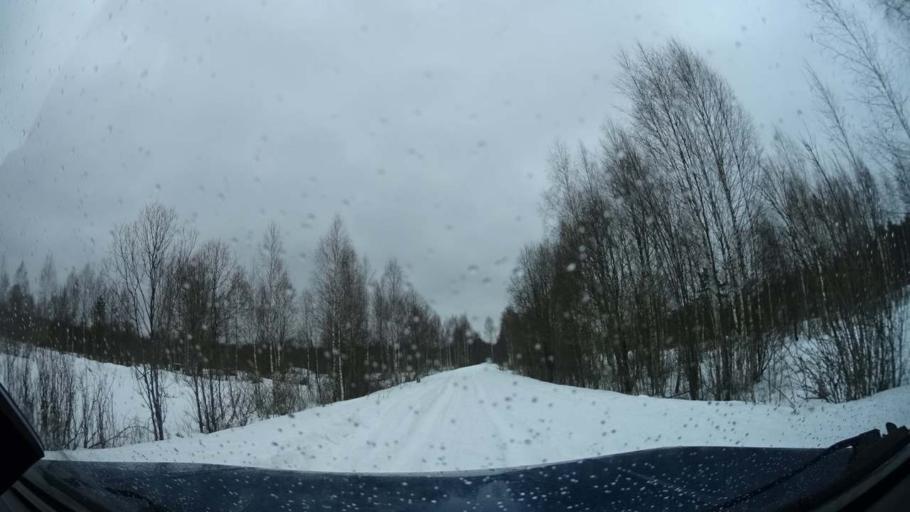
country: RU
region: Tverskaya
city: Gorodnya
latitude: 56.7941
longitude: 36.3654
